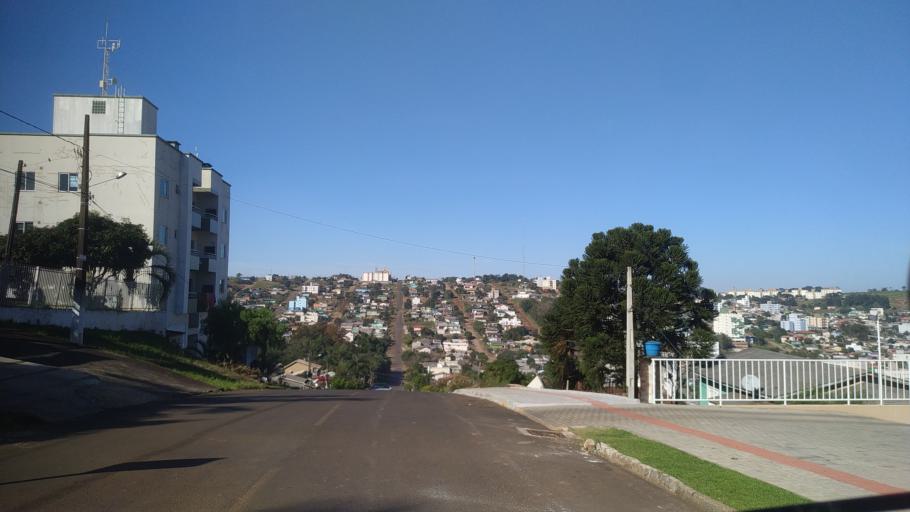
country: BR
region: Santa Catarina
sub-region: Chapeco
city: Chapeco
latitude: -27.1107
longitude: -52.5960
